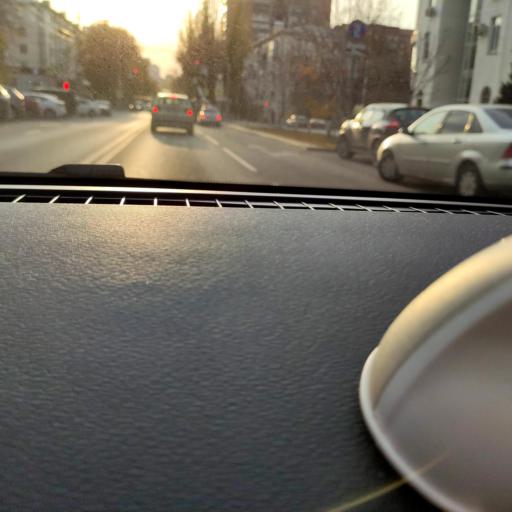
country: RU
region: Samara
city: Samara
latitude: 53.2087
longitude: 50.1250
